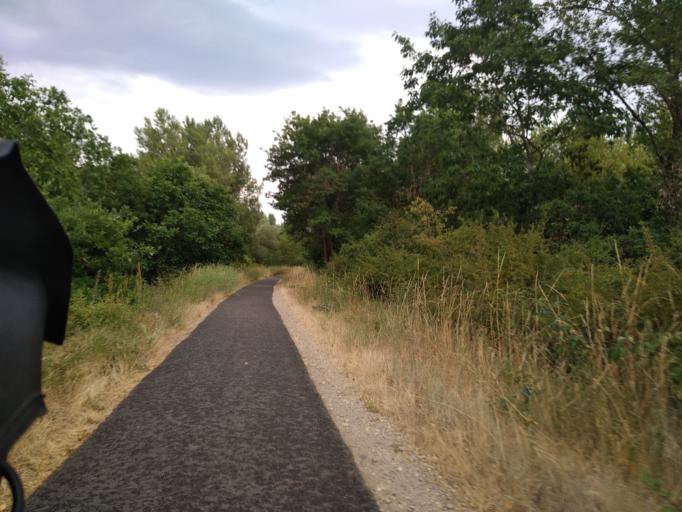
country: FR
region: Auvergne
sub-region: Departement de l'Allier
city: Varennes-sur-Allier
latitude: 46.3478
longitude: 3.3480
